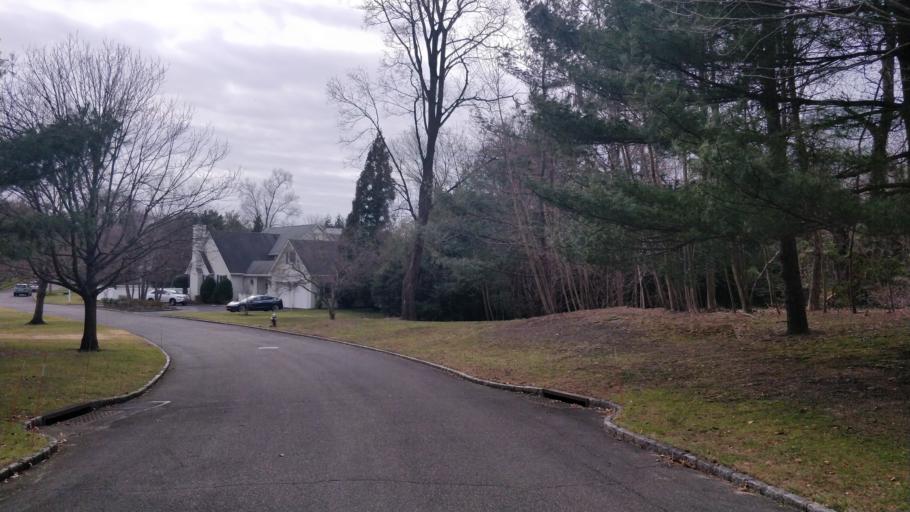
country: US
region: New York
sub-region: Nassau County
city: Locust Valley
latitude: 40.8678
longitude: -73.5992
